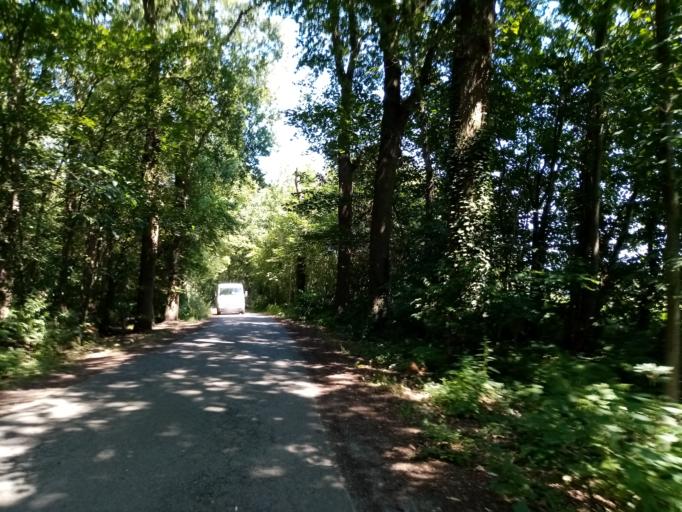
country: NL
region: North Brabant
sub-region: Gemeente Breda
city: Breda
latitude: 51.6110
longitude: 4.7320
